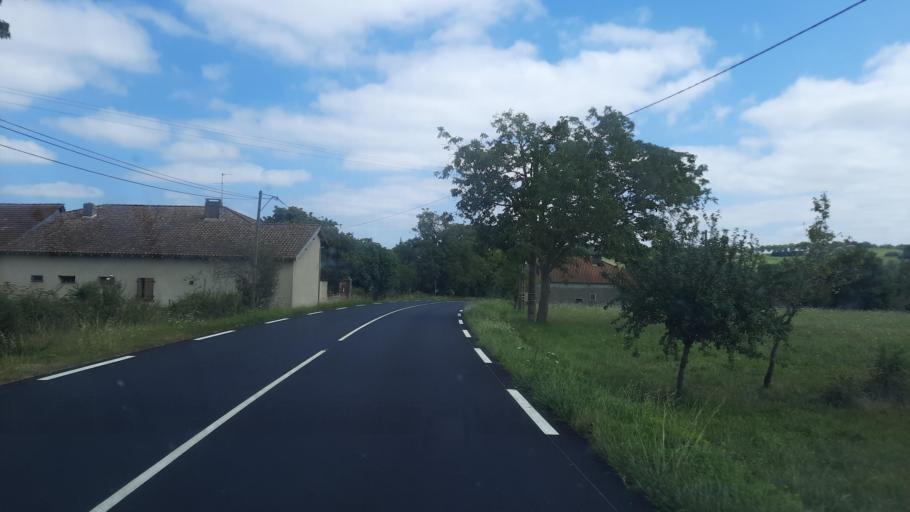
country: FR
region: Midi-Pyrenees
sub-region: Departement de la Haute-Garonne
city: Boulogne-sur-Gesse
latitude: 43.2956
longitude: 0.6241
